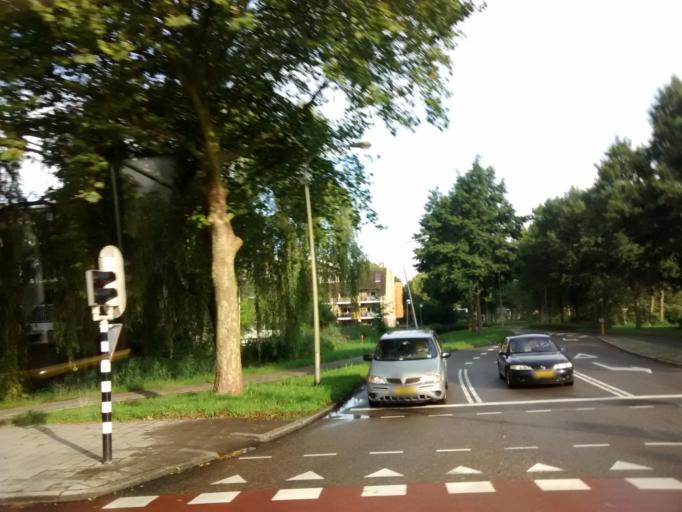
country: NL
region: South Holland
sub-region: Gemeente Gouda
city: Bloemendaal
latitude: 52.0226
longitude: 4.6932
